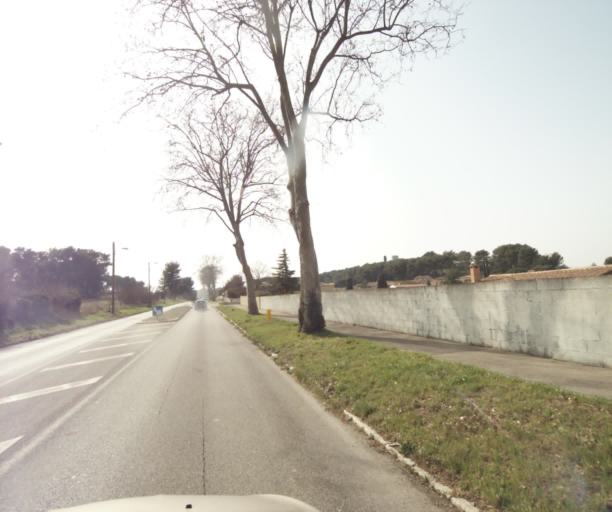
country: FR
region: Provence-Alpes-Cote d'Azur
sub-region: Departement des Bouches-du-Rhone
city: Septemes-les-Vallons
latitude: 43.4159
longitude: 5.3758
